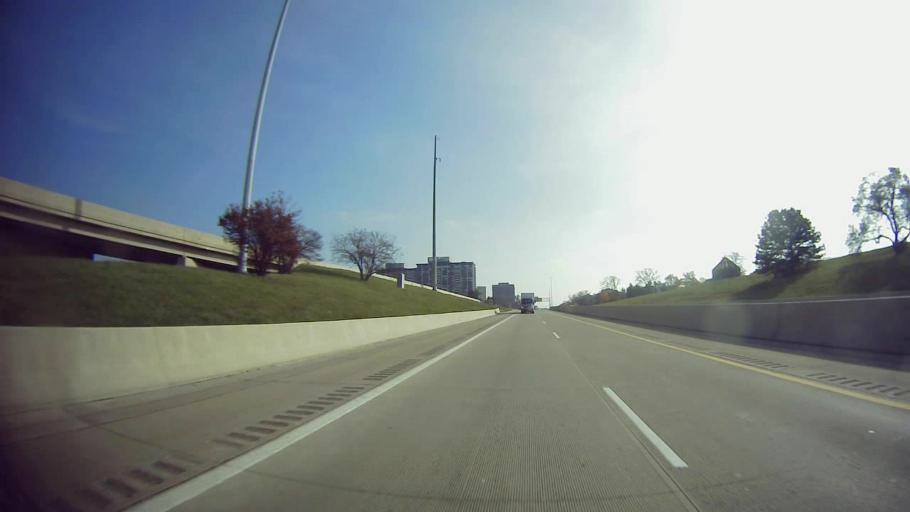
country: US
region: Michigan
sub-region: Oakland County
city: Southfield
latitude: 42.4568
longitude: -83.2183
